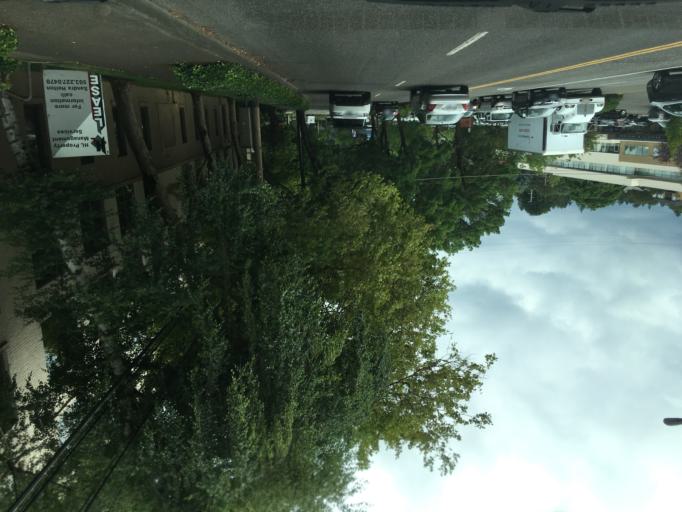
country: US
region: Oregon
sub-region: Multnomah County
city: Portland
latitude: 45.4853
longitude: -122.6752
